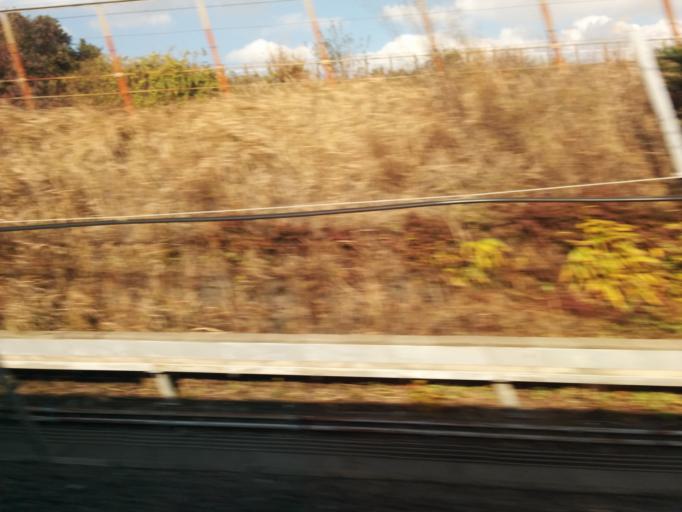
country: JP
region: Aichi
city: Toyohashi
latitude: 34.7303
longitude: 137.4202
